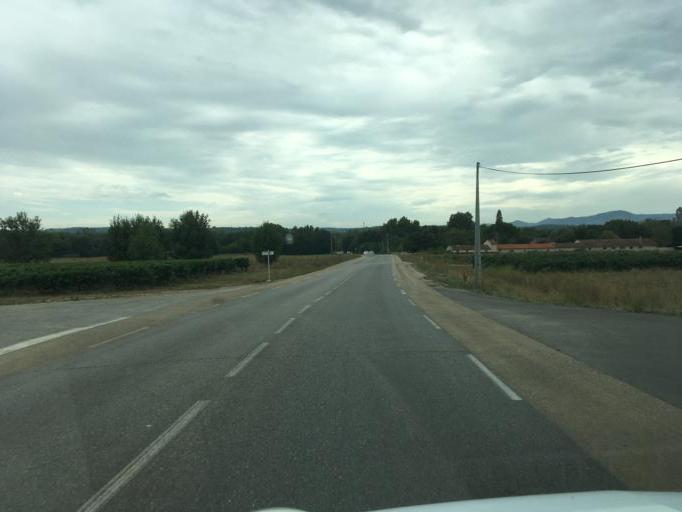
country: FR
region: Provence-Alpes-Cote d'Azur
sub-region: Departement des Bouches-du-Rhone
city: Rousset
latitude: 43.4750
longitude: 5.6188
